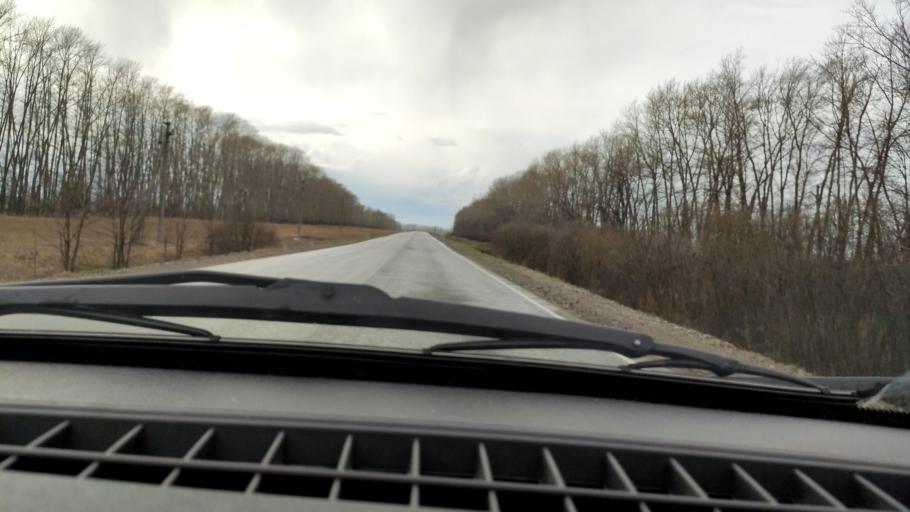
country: RU
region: Bashkortostan
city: Alekseyevka
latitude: 55.0604
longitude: 55.1070
